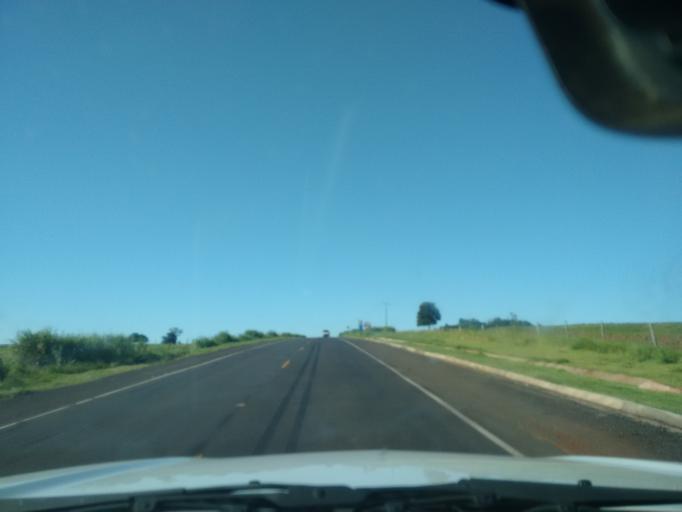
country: PY
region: Canindeyu
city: Salto del Guaira
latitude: -23.9799
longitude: -54.3310
